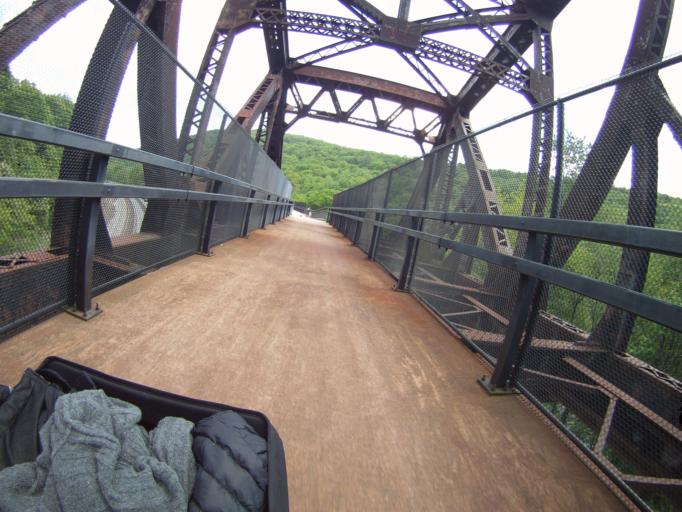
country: US
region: Pennsylvania
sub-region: Somerset County
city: Meyersdale
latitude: 39.8110
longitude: -78.9958
